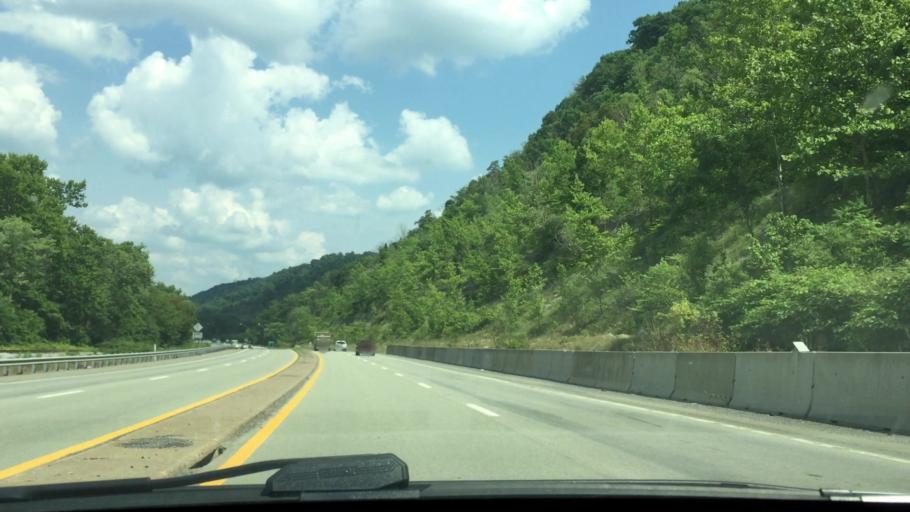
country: US
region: West Virginia
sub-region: Marshall County
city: Moundsville
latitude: 39.9057
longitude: -80.7662
